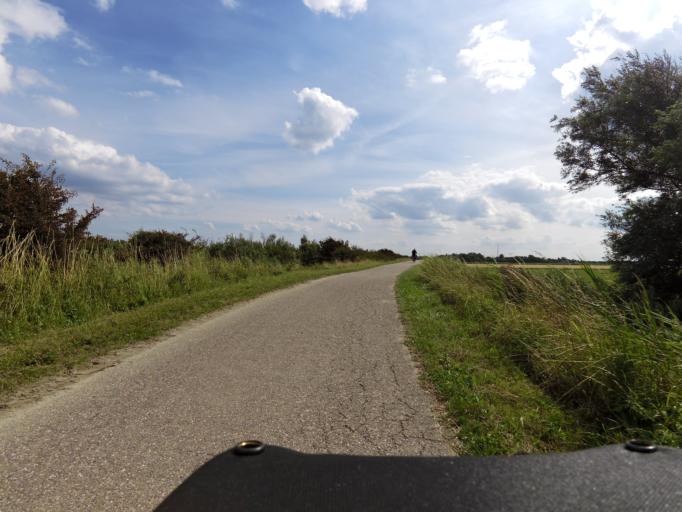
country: NL
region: South Holland
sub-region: Gemeente Goeree-Overflakkee
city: Ouddorp
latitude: 51.8202
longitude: 3.8966
